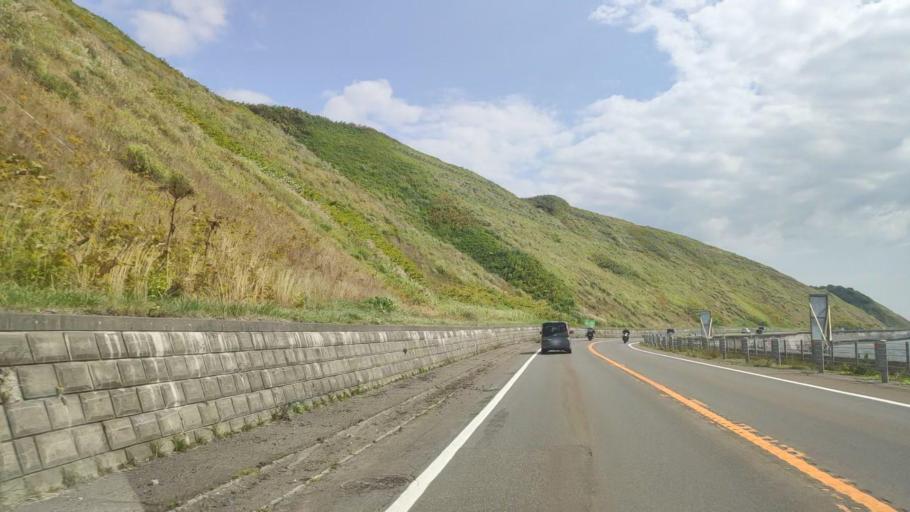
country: JP
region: Hokkaido
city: Rumoi
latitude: 44.2427
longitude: 141.6580
